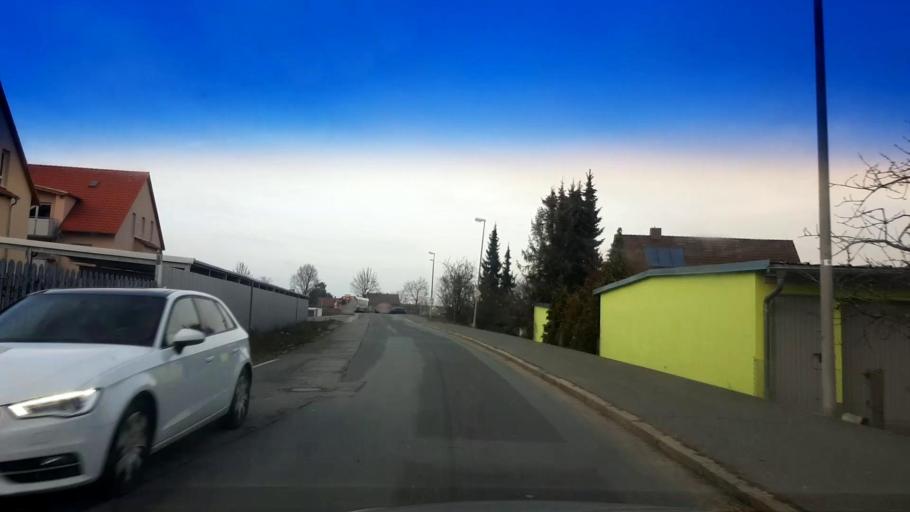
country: DE
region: Bavaria
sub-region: Upper Franconia
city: Hirschaid
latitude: 49.8095
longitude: 10.9812
